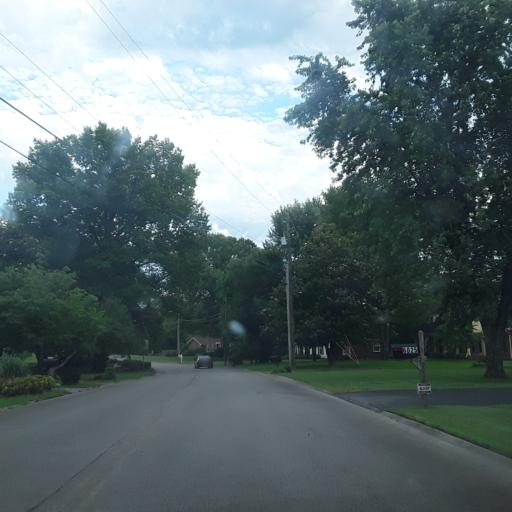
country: US
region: Tennessee
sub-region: Wilson County
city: Green Hill
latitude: 36.1648
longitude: -86.5866
